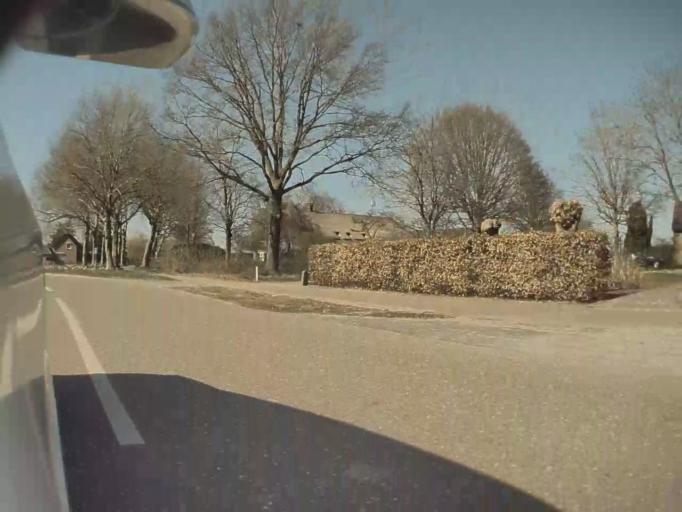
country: NL
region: North Brabant
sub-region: Gemeente Uden
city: Uden
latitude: 51.6953
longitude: 5.5803
